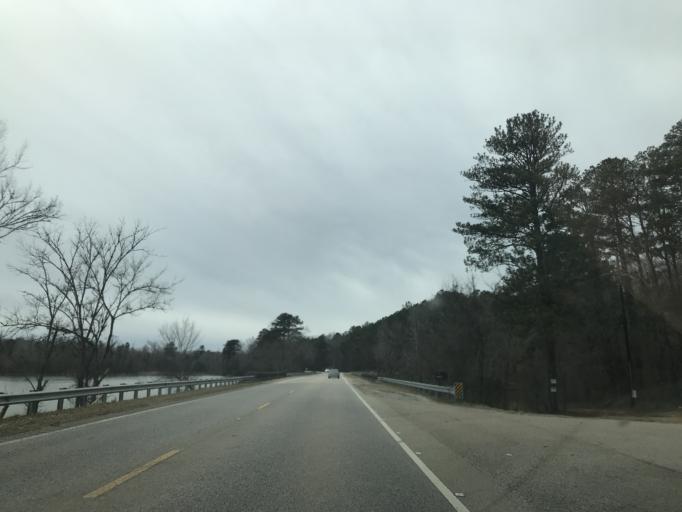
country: US
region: Alabama
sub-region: Shelby County
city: Brook Highland
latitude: 33.4487
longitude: -86.6543
